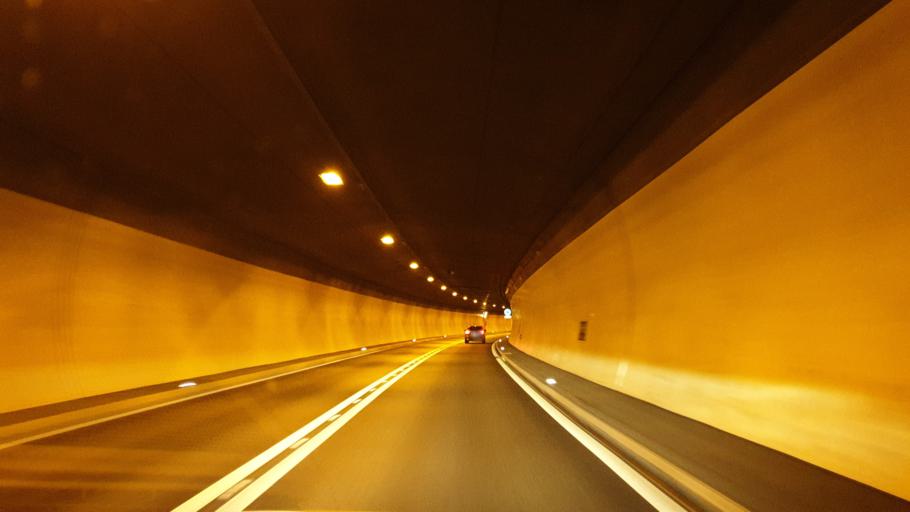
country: CH
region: Uri
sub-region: Uri
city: Flueelen
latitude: 46.9006
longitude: 8.6269
